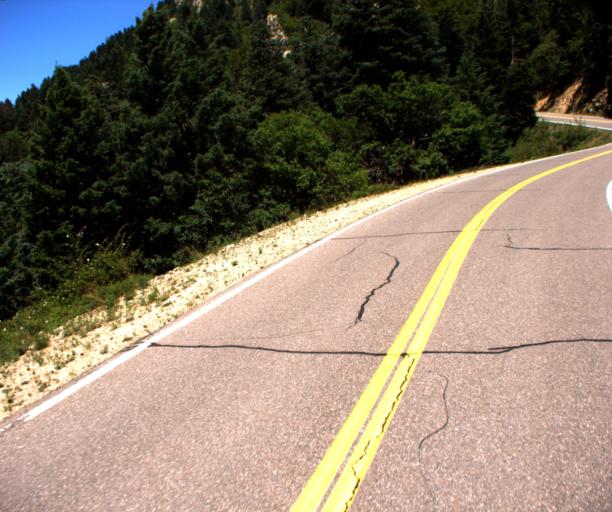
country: US
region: Arizona
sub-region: Graham County
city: Swift Trail Junction
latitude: 32.6420
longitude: -109.8488
